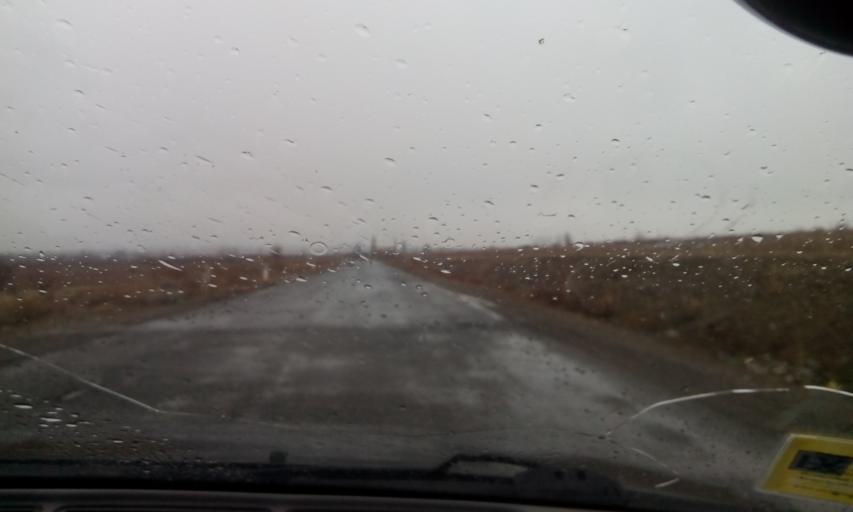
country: AM
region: Armavir
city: Nalbandyan
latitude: 40.0679
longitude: 43.9857
